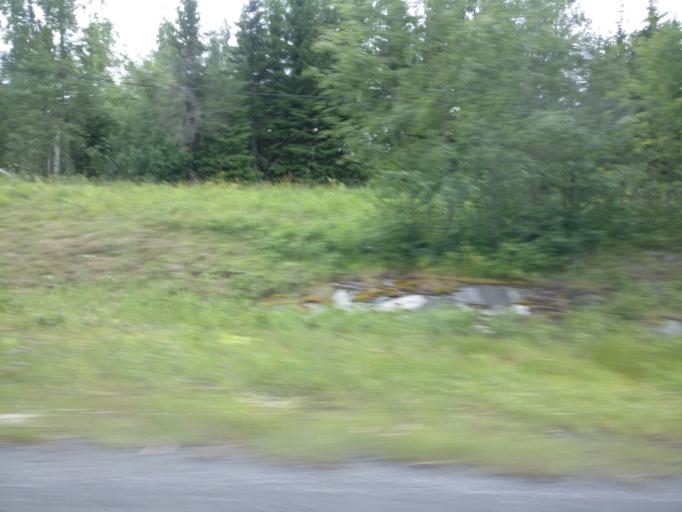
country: FI
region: Northern Savo
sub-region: Kuopio
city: Kuopio
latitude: 62.9540
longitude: 27.8718
